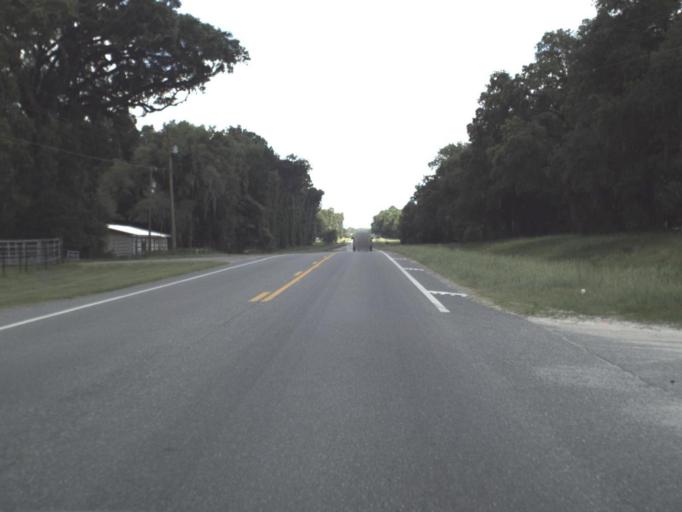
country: US
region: Florida
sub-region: Columbia County
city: Lake City
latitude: 30.1301
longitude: -82.6258
